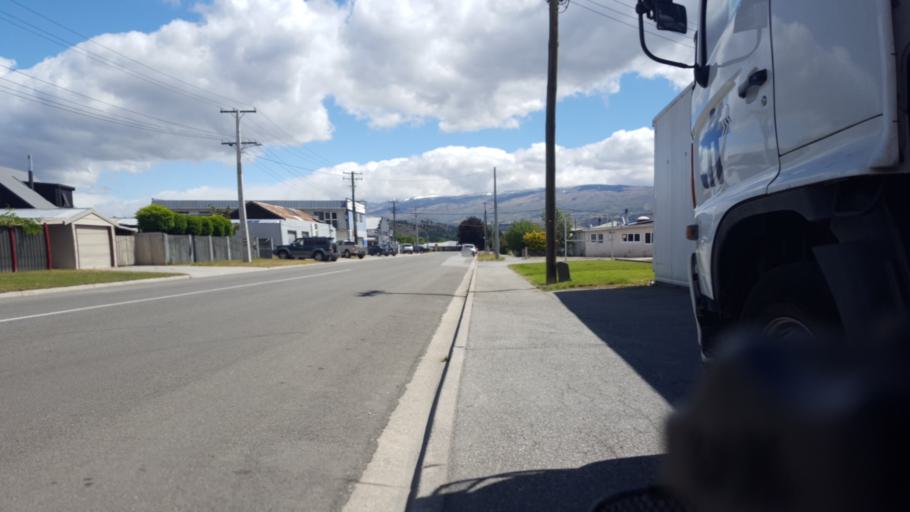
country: NZ
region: Otago
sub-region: Queenstown-Lakes District
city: Wanaka
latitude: -45.2465
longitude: 169.3938
